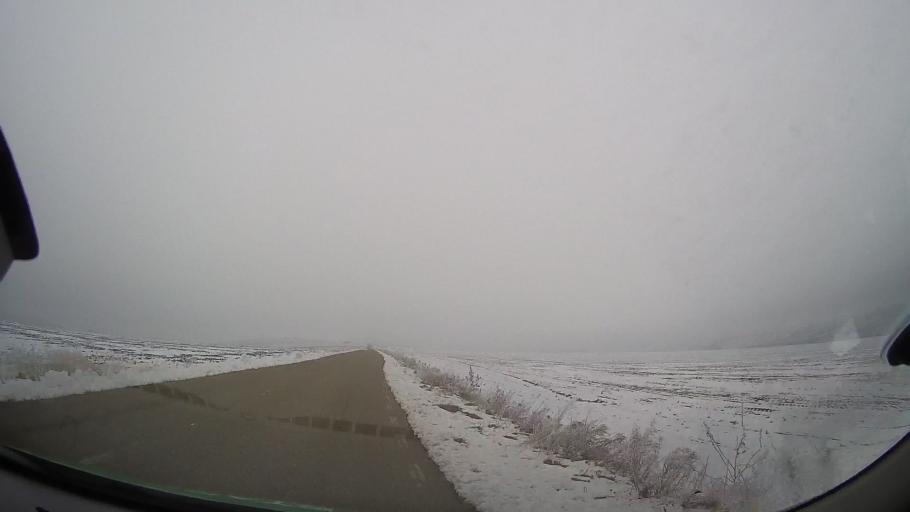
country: RO
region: Vaslui
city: Coroiesti
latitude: 46.2207
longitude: 27.4789
